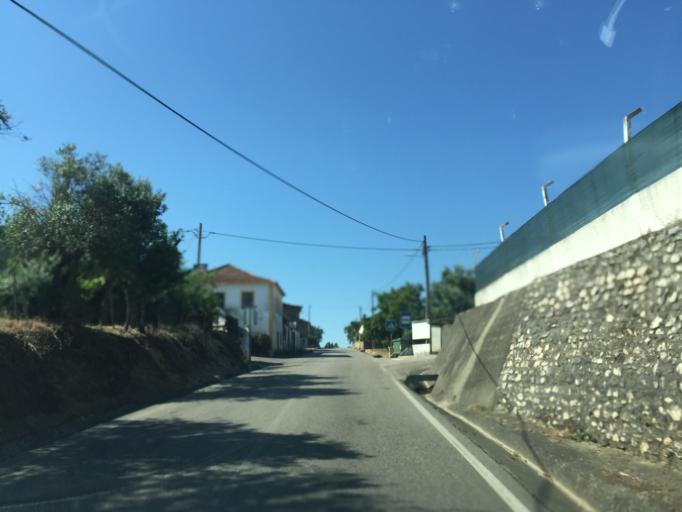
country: PT
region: Santarem
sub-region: Tomar
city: Tomar
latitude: 39.5832
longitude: -8.3275
